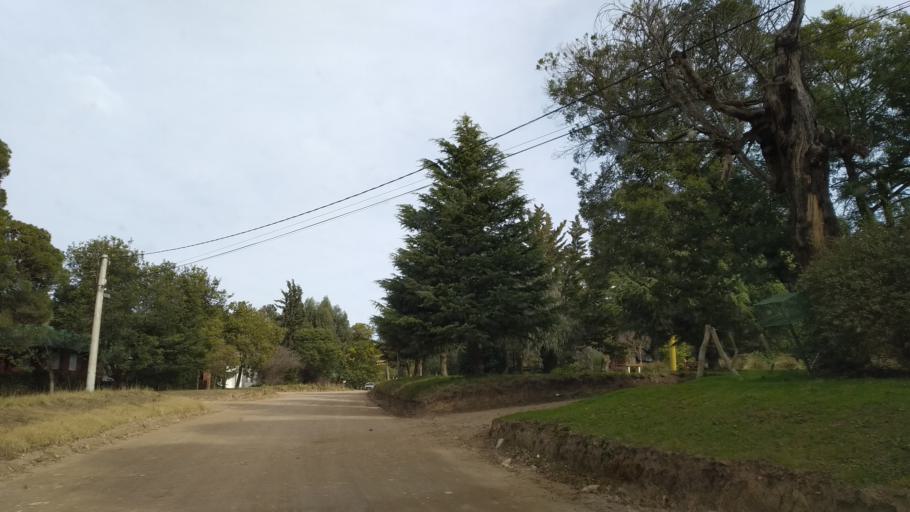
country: AR
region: Buenos Aires
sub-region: Partido de Tornquist
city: Tornquist
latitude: -38.0830
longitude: -61.9284
